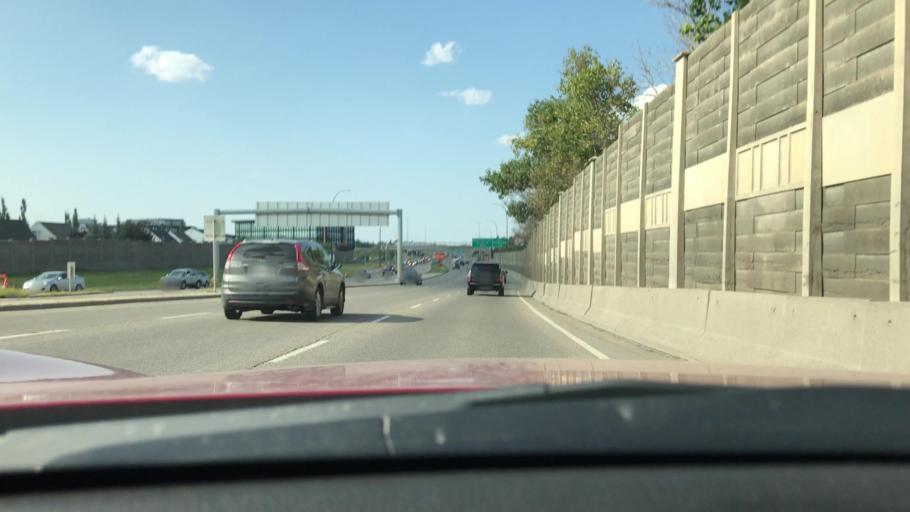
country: CA
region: Alberta
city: Calgary
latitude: 51.0020
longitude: -114.1179
